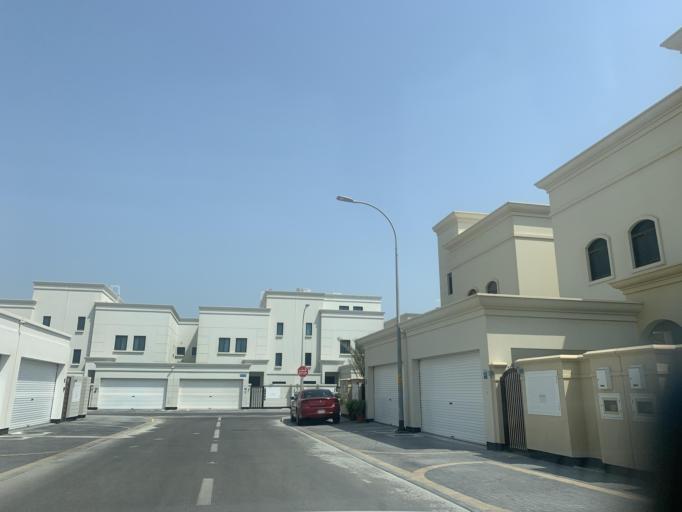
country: BH
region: Muharraq
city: Al Muharraq
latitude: 26.3016
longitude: 50.6316
